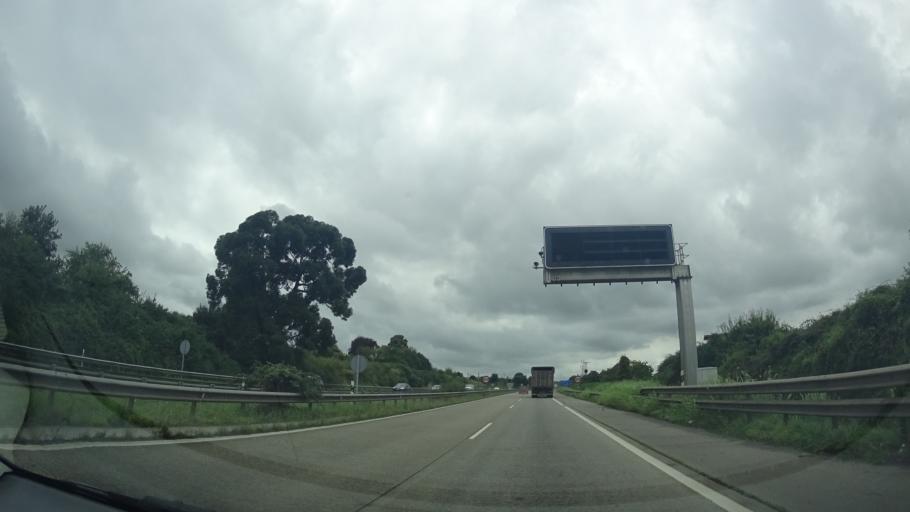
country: ES
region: Asturias
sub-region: Province of Asturias
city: Natahoyo
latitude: 43.5294
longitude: -5.6860
